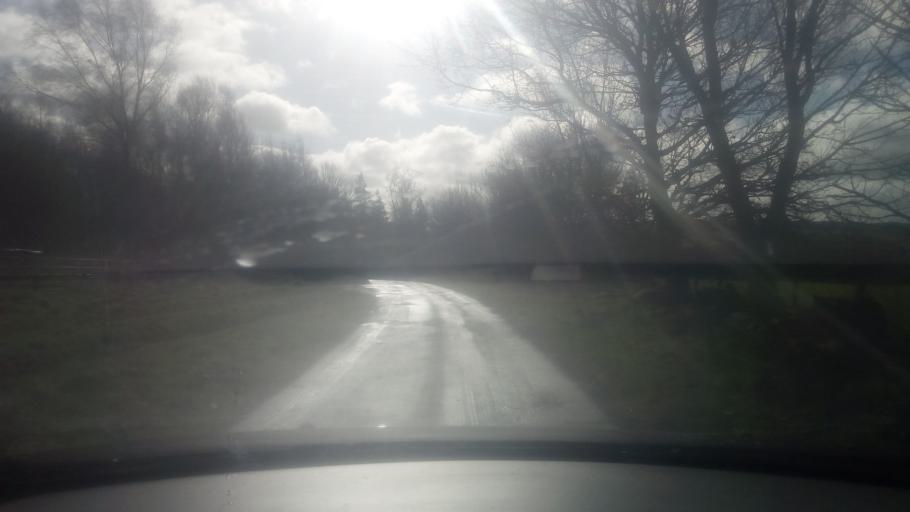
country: GB
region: Scotland
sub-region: The Scottish Borders
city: Jedburgh
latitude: 55.5185
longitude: -2.5708
